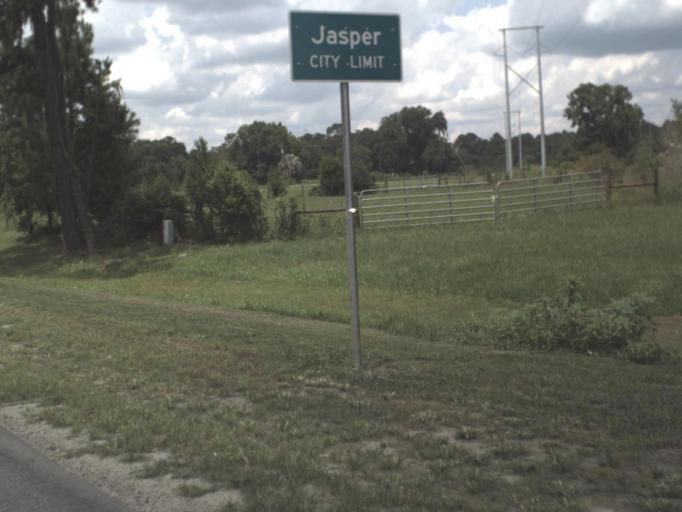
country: US
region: Florida
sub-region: Hamilton County
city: Jasper
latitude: 30.5082
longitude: -82.9461
